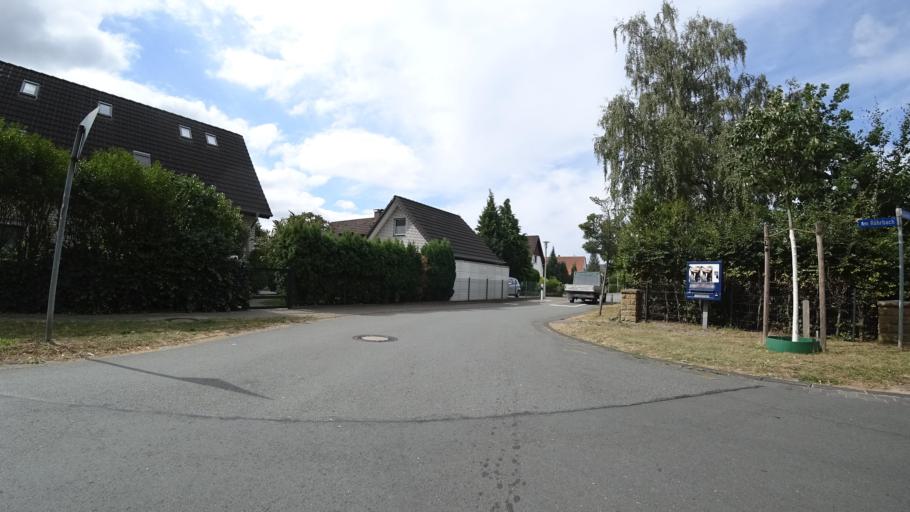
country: DE
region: North Rhine-Westphalia
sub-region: Regierungsbezirk Detmold
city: Verl
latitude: 51.9418
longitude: 8.4835
